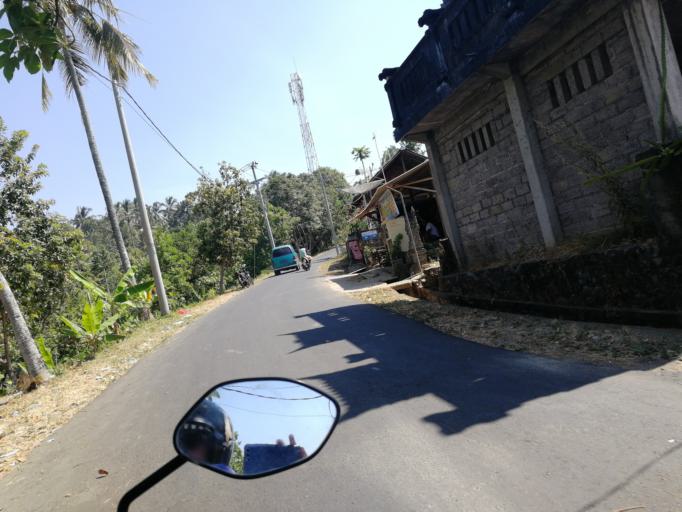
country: ID
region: Bali
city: Banjar Kedisan
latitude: -8.1558
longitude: 115.3070
